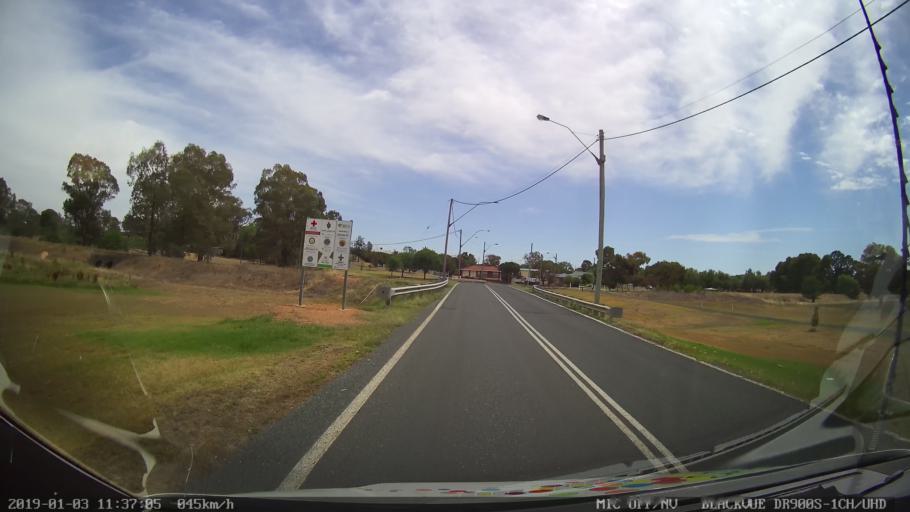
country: AU
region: New South Wales
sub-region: Weddin
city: Grenfell
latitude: -33.9052
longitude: 148.1604
